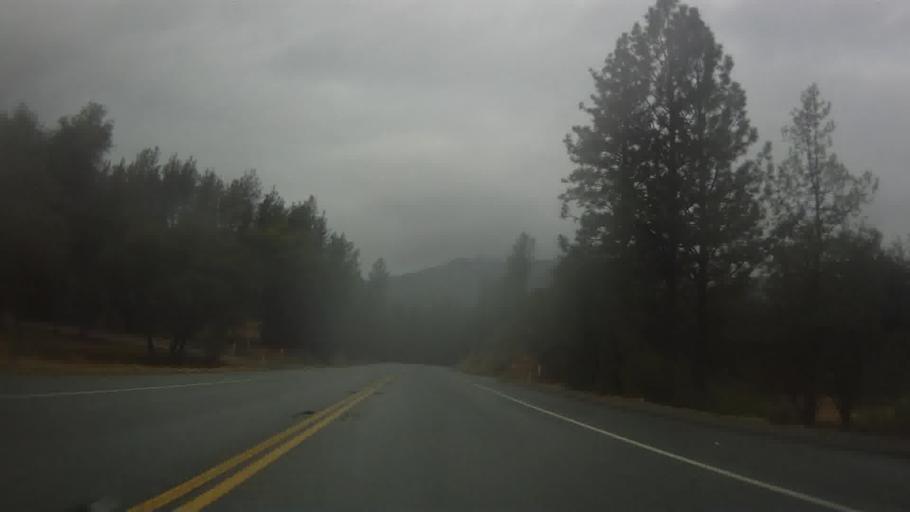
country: US
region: California
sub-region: Shasta County
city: Shasta
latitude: 40.5908
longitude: -122.4769
